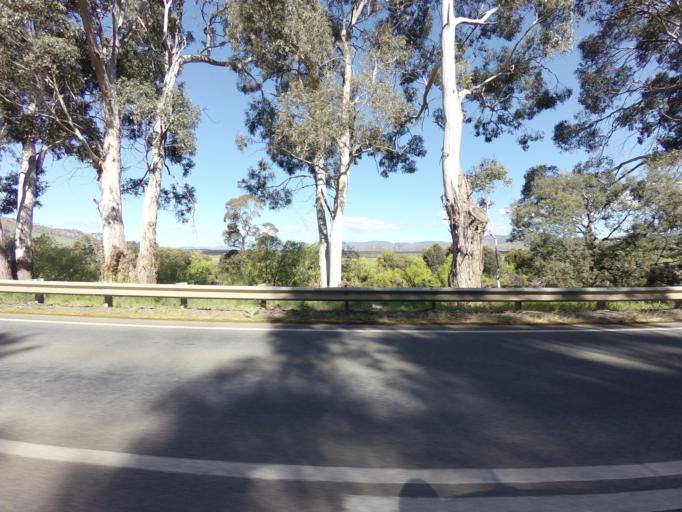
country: AU
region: Tasmania
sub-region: Derwent Valley
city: New Norfolk
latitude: -42.7345
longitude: 146.9642
